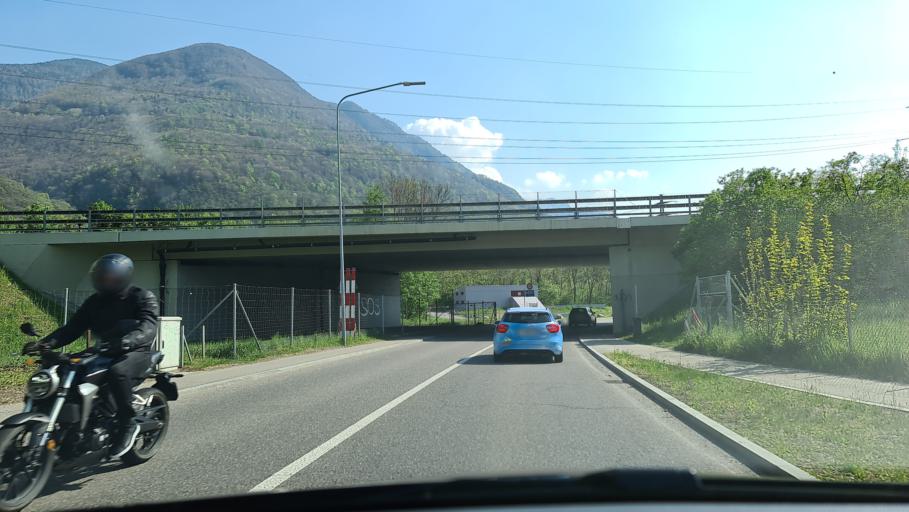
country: CH
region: Ticino
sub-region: Bellinzona District
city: Lumino
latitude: 46.2222
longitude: 9.0473
